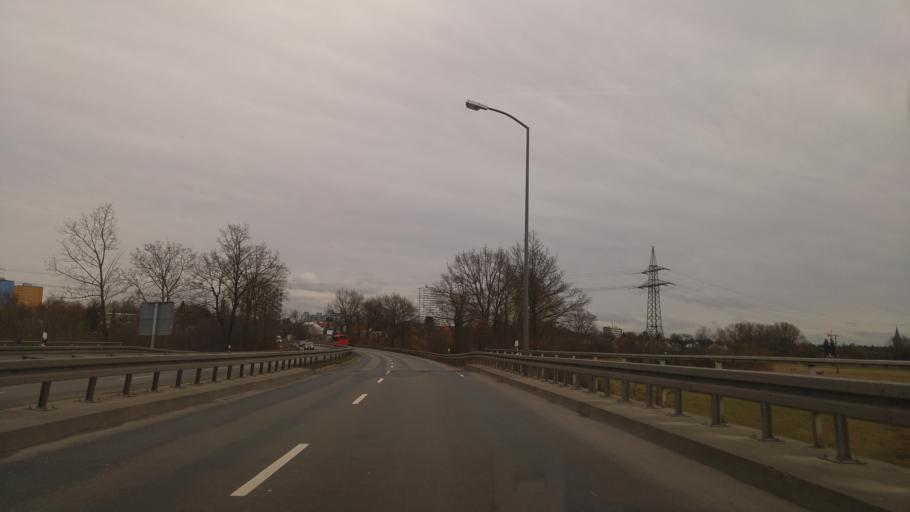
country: DE
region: Bavaria
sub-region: Regierungsbezirk Mittelfranken
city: Erlangen
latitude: 49.5842
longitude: 10.9804
